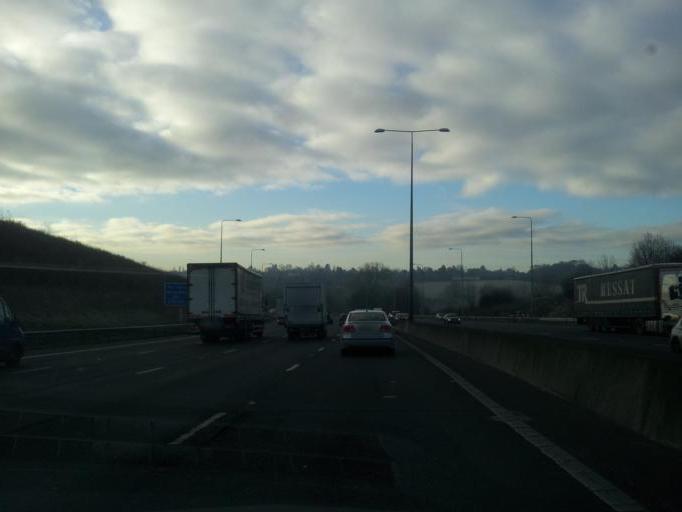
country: GB
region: England
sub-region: Hertfordshire
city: Chorleywood
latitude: 51.6669
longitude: -0.4925
